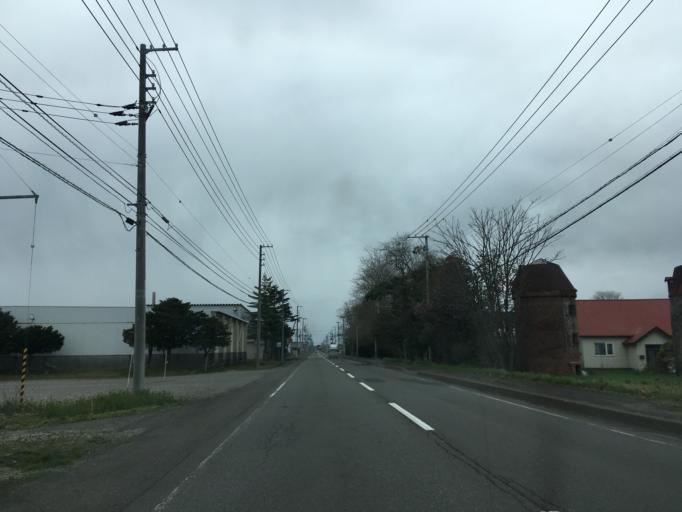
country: JP
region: Hokkaido
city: Chitose
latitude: 42.9402
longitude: 141.8047
